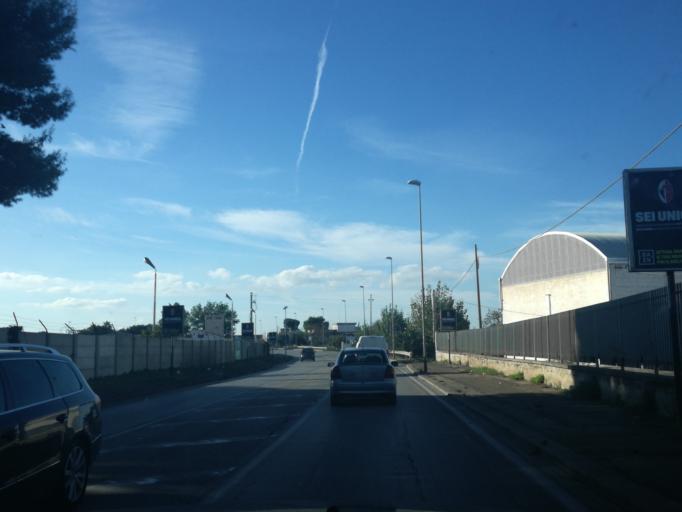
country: IT
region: Apulia
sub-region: Provincia di Bari
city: Bari
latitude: 41.1239
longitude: 16.8324
